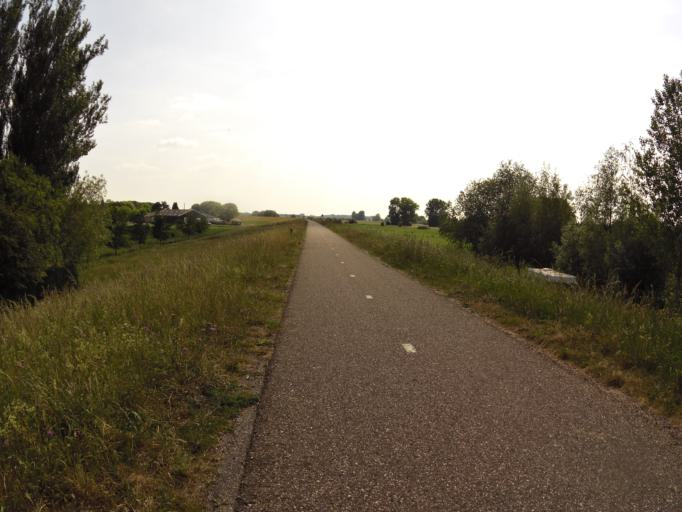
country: NL
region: Gelderland
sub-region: Gemeente Maasdriel
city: Heerewaarden
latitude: 51.8213
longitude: 5.3887
